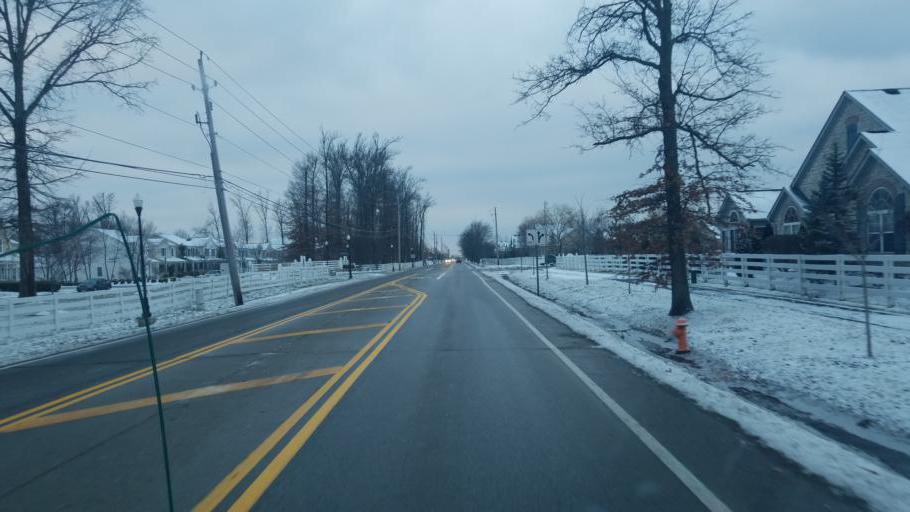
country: US
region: Ohio
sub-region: Franklin County
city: New Albany
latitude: 40.0641
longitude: -82.8516
